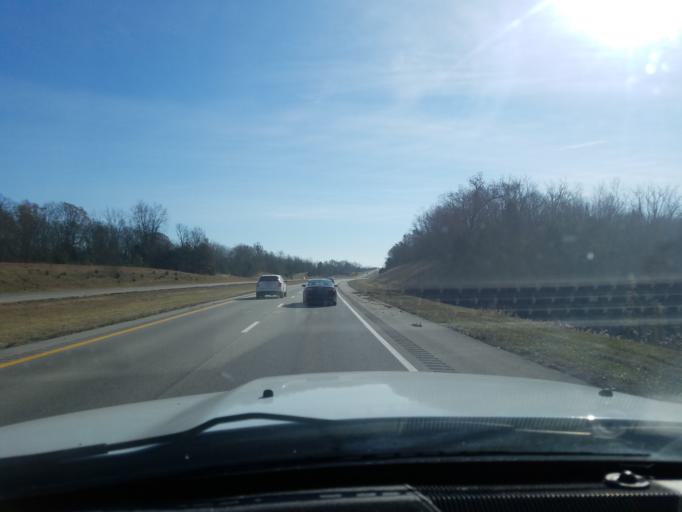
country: US
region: Ohio
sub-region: Adams County
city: Winchester
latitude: 38.9471
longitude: -83.6796
